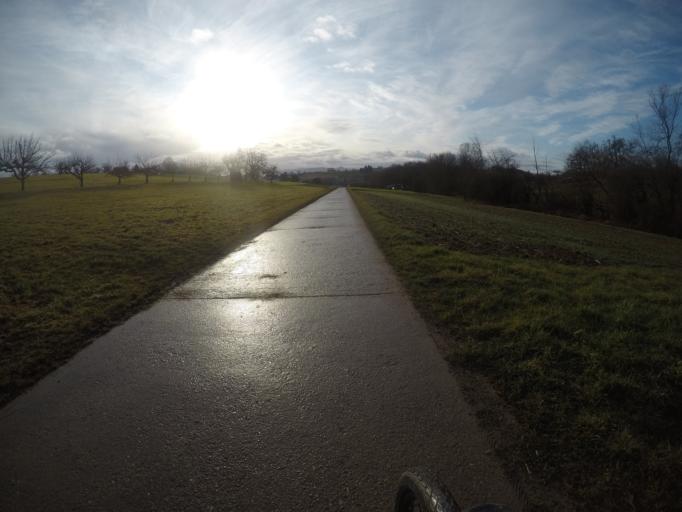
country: DE
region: Baden-Wuerttemberg
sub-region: Regierungsbezirk Stuttgart
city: Unterensingen
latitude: 48.6566
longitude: 9.3429
